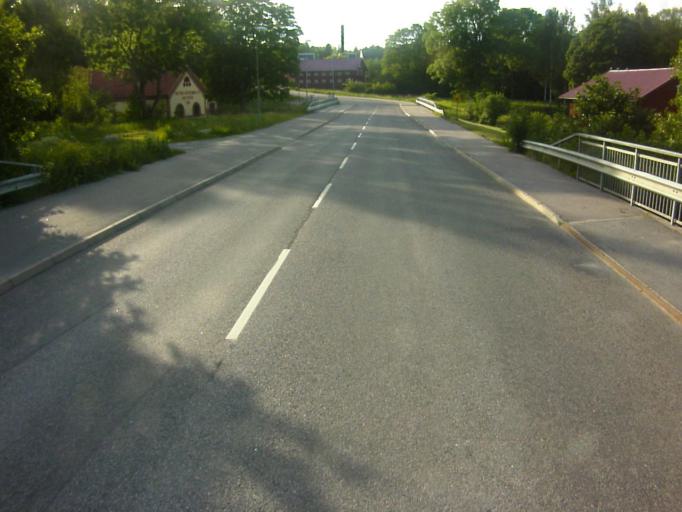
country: SE
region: Soedermanland
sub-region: Eskilstuna Kommun
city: Skogstorp
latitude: 59.3311
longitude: 16.4772
